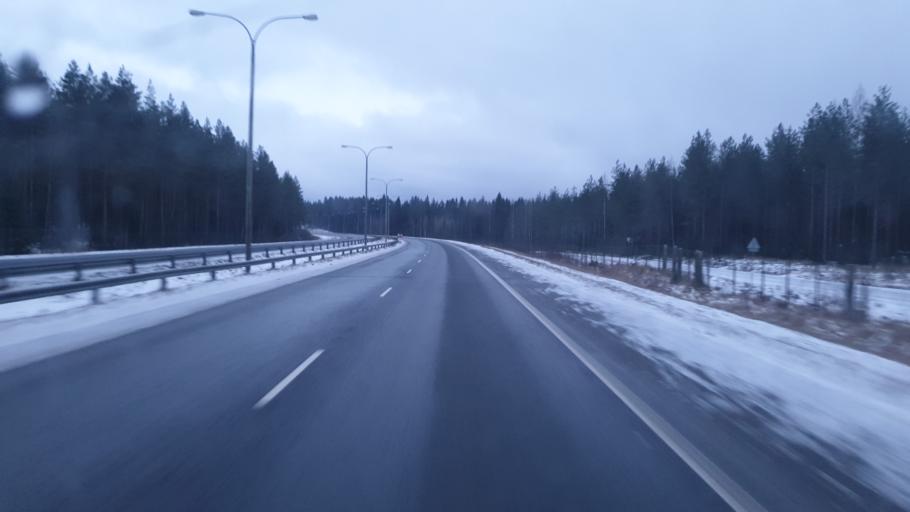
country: FI
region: Northern Savo
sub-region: Kuopio
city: Siilinjaervi
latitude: 63.0071
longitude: 27.6801
